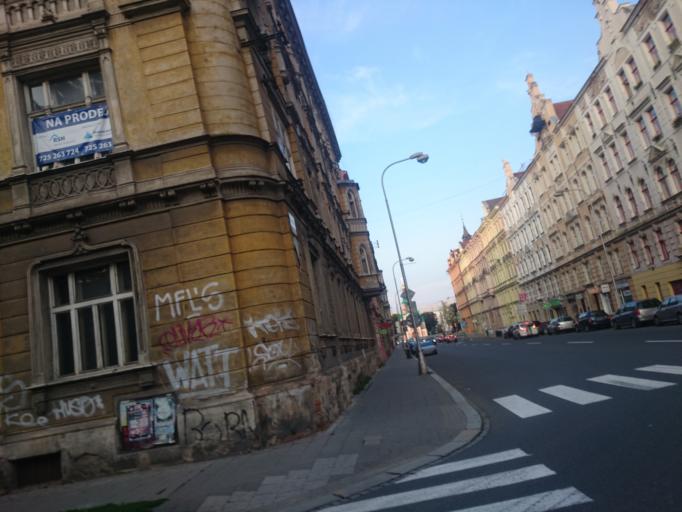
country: CZ
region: Olomoucky
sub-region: Okres Olomouc
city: Olomouc
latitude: 49.5973
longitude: 17.2648
